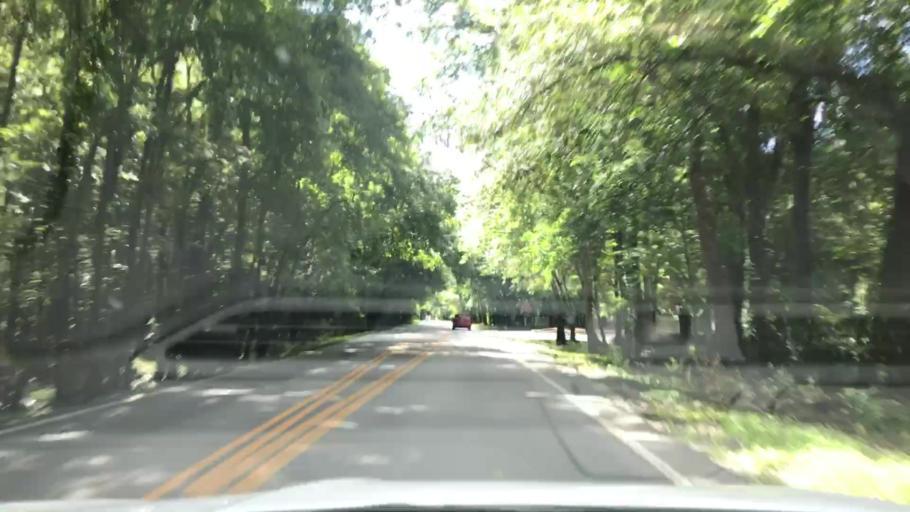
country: US
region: South Carolina
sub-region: Charleston County
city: Shell Point
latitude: 32.8599
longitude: -80.0773
